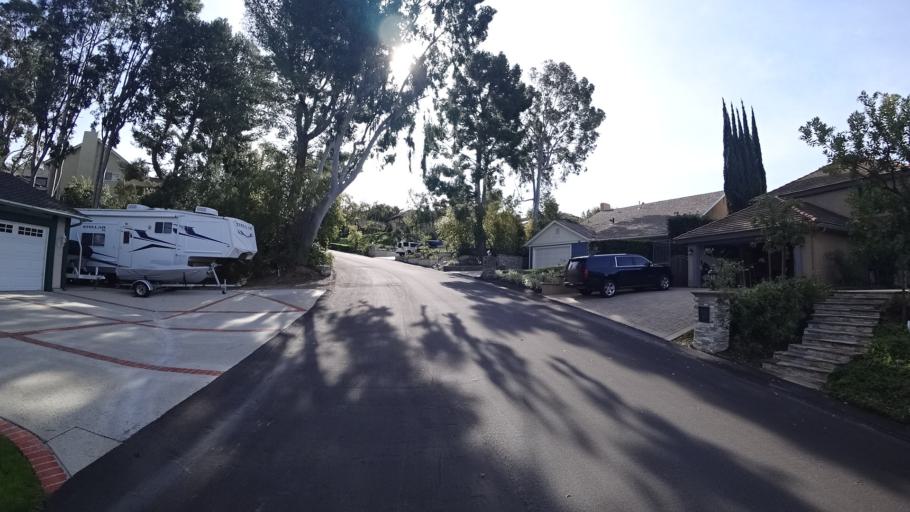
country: US
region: California
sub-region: Orange County
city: Yorba Linda
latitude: 33.8578
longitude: -117.7628
